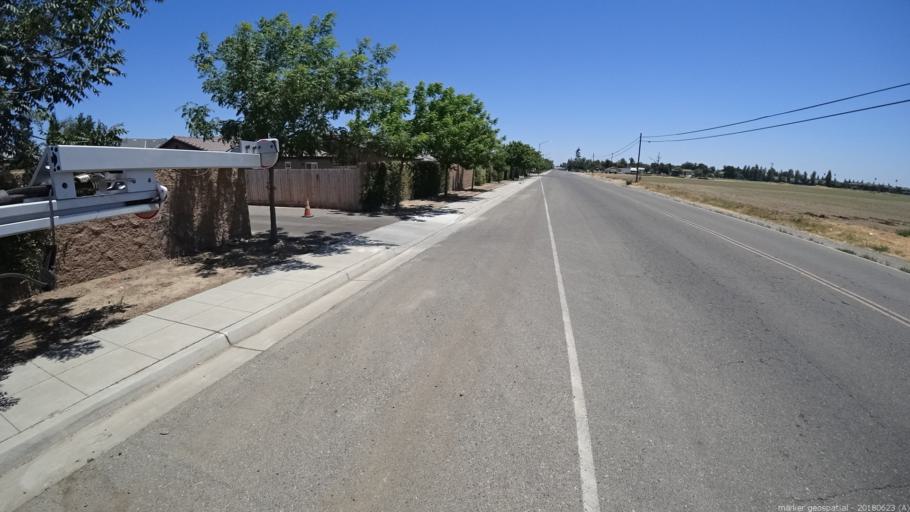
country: US
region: California
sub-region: Madera County
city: Chowchilla
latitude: 37.1128
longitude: -120.2836
